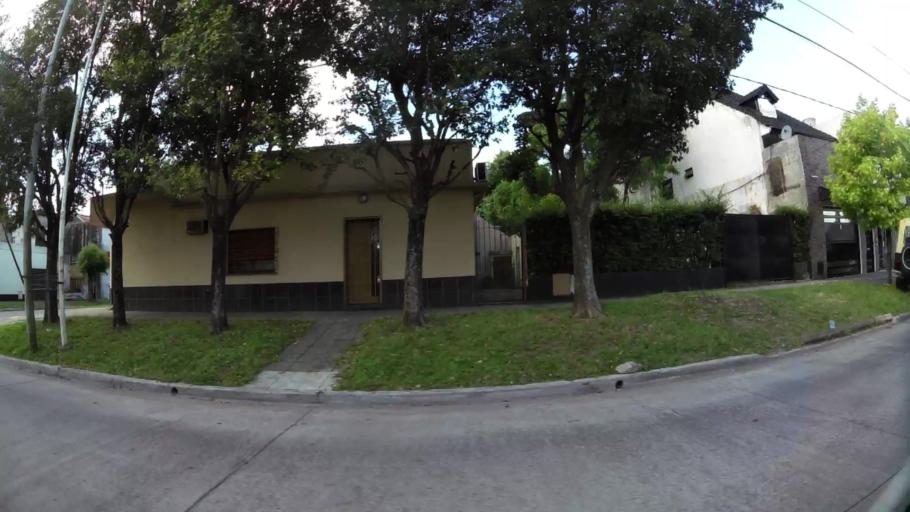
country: AR
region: Buenos Aires
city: San Justo
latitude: -34.6732
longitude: -58.5770
